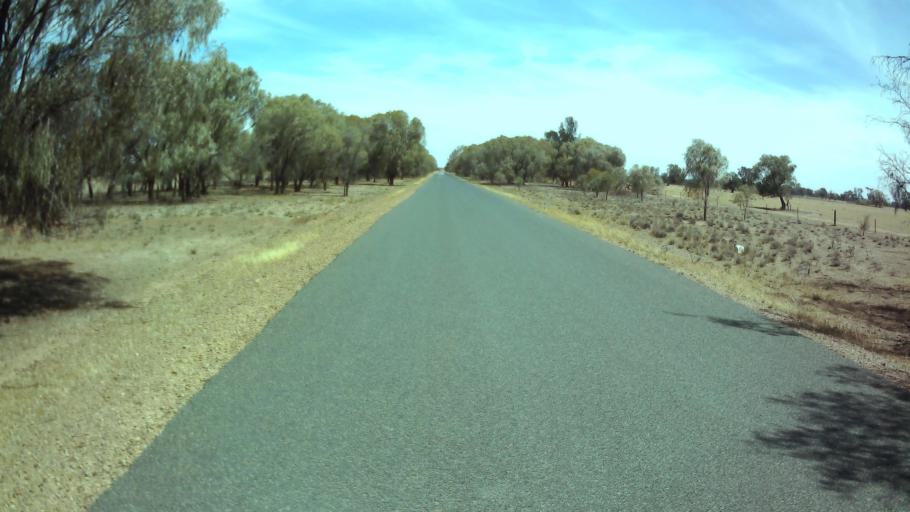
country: AU
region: New South Wales
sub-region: Weddin
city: Grenfell
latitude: -33.8722
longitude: 147.7445
